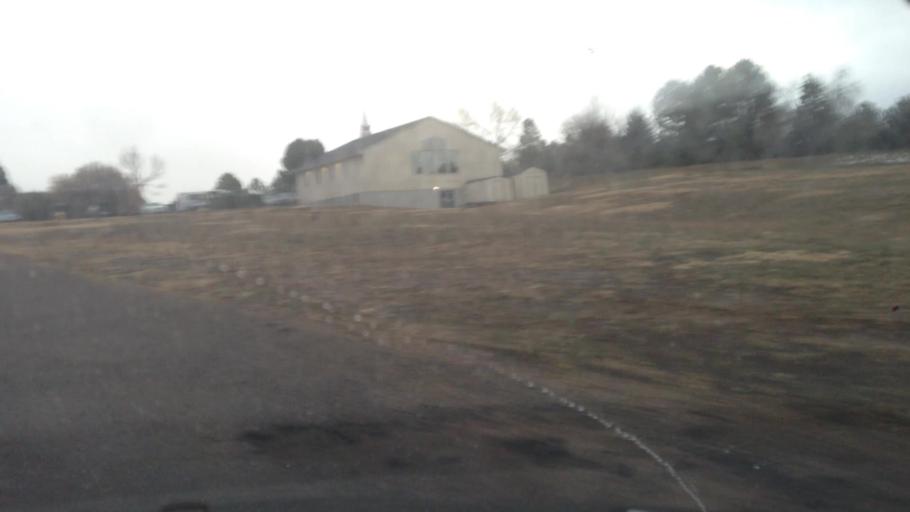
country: US
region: Colorado
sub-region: Arapahoe County
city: Castlewood
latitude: 39.6239
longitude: -104.8823
